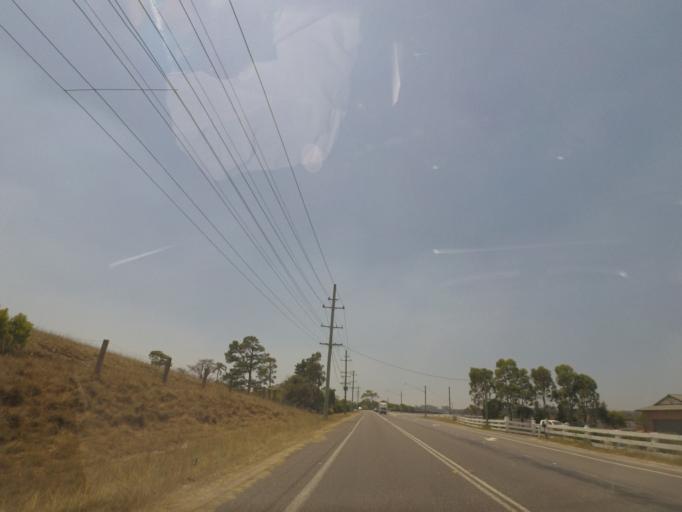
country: AU
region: New South Wales
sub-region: Port Stephens Shire
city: Medowie
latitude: -32.8027
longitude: 151.8846
